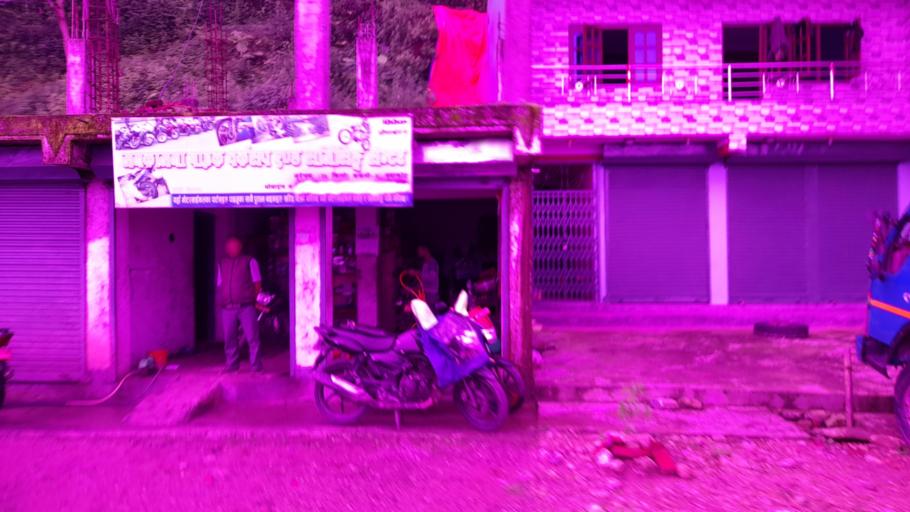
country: NP
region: Central Region
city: Kirtipur
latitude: 27.8280
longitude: 85.2094
